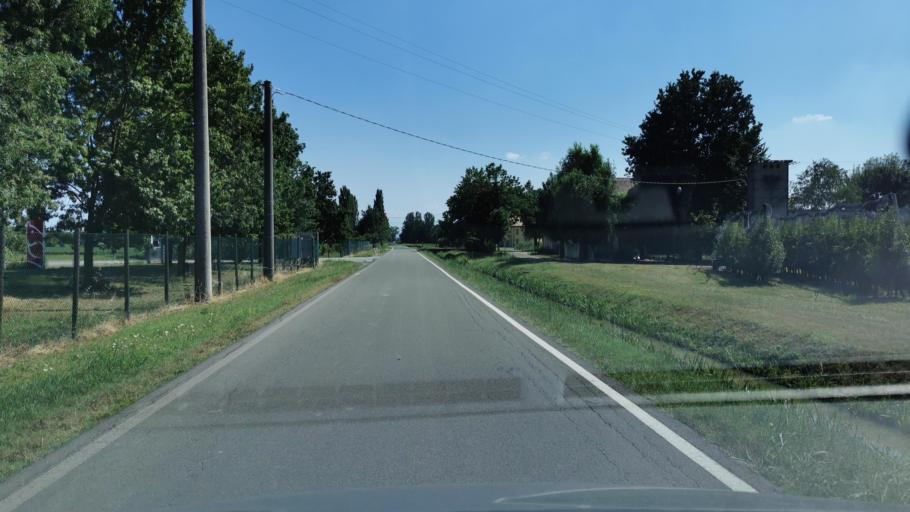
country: IT
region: Emilia-Romagna
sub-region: Provincia di Modena
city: Limidi
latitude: 44.7788
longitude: 10.9184
